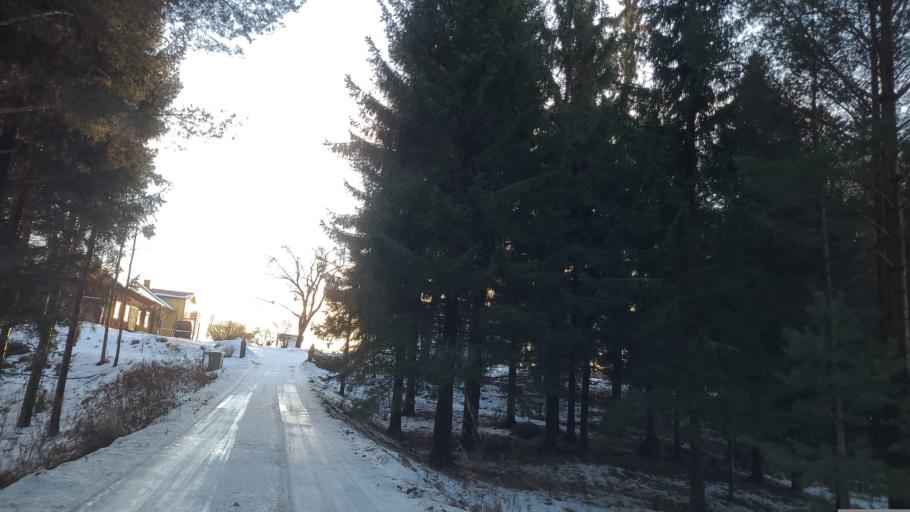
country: SE
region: Gaevleborg
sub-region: Bollnas Kommun
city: Bollnas
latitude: 61.3502
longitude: 16.4095
